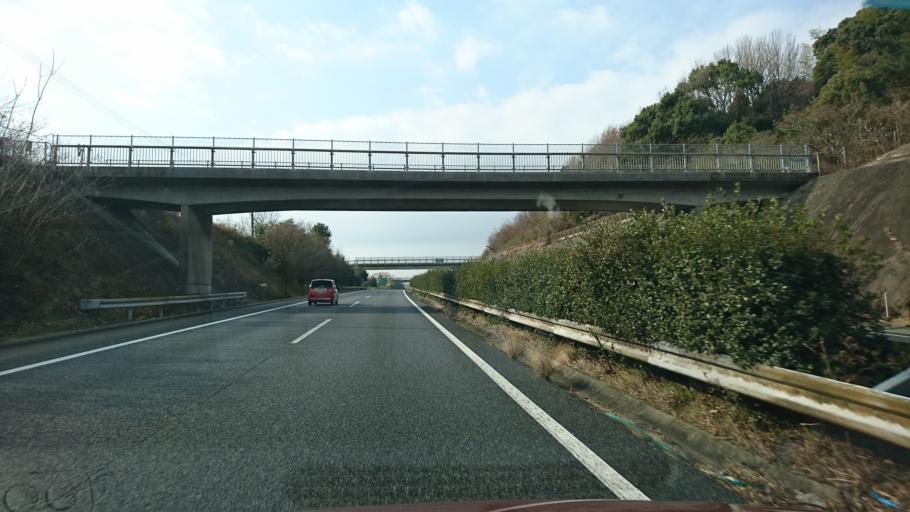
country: JP
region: Okayama
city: Kamogatacho-kamogata
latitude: 34.5739
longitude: 133.6704
